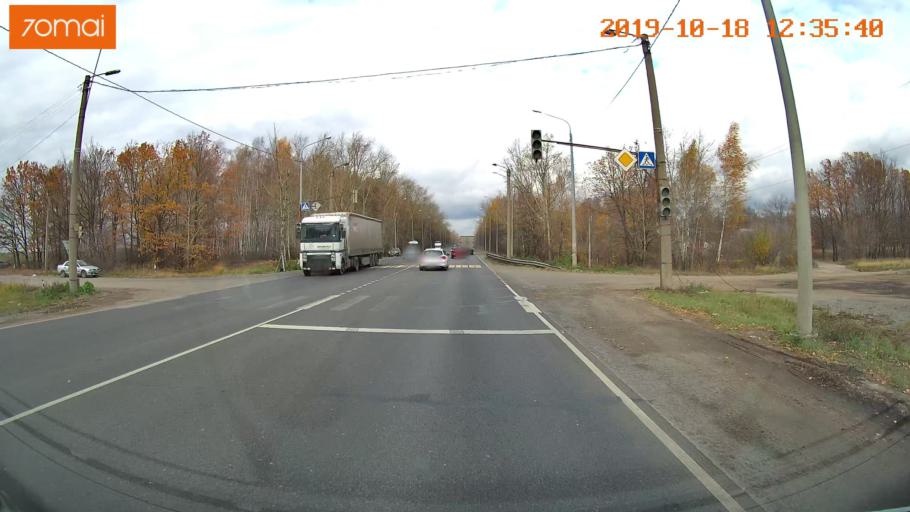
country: RU
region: Rjazan
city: Ryazan'
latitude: 54.6268
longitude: 39.6353
